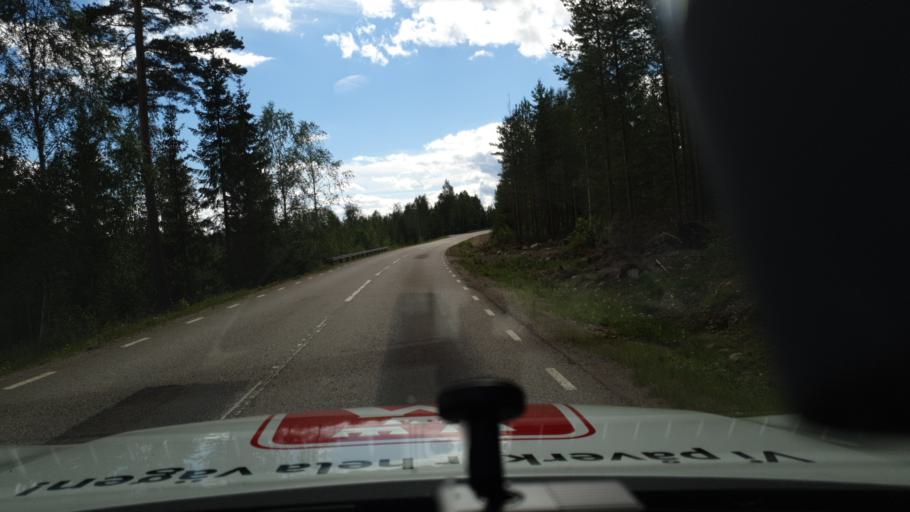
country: NO
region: Hedmark
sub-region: Trysil
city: Innbygda
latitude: 61.0324
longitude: 12.5833
